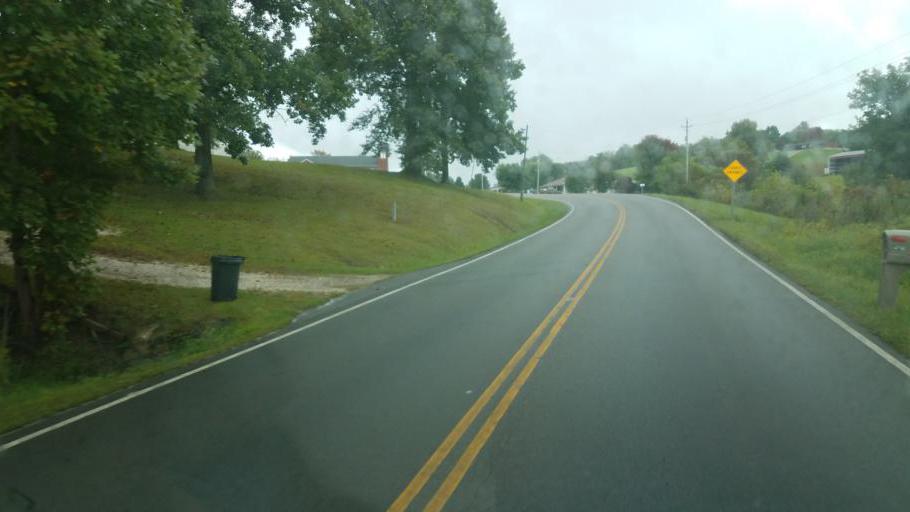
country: US
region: Ohio
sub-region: Scioto County
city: Wheelersburg
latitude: 38.7686
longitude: -82.8068
